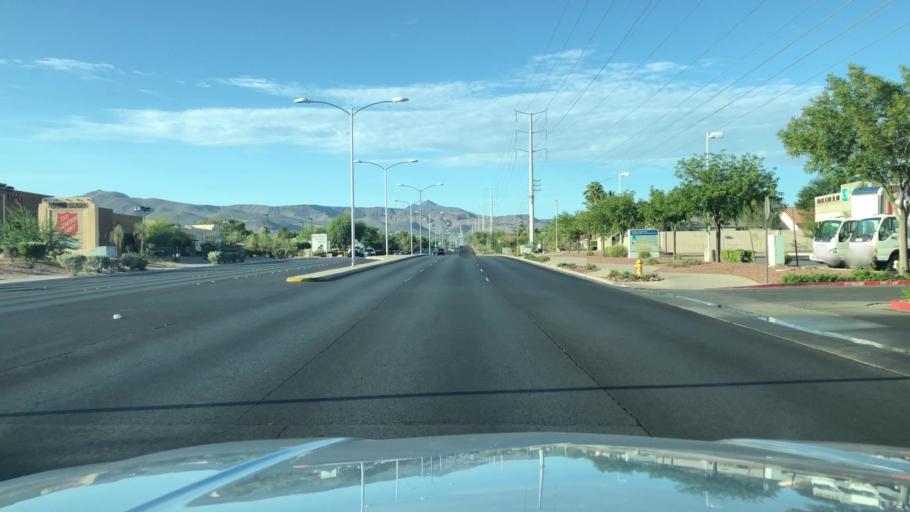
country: US
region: Nevada
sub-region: Clark County
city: Whitney
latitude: 36.0545
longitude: -115.0464
